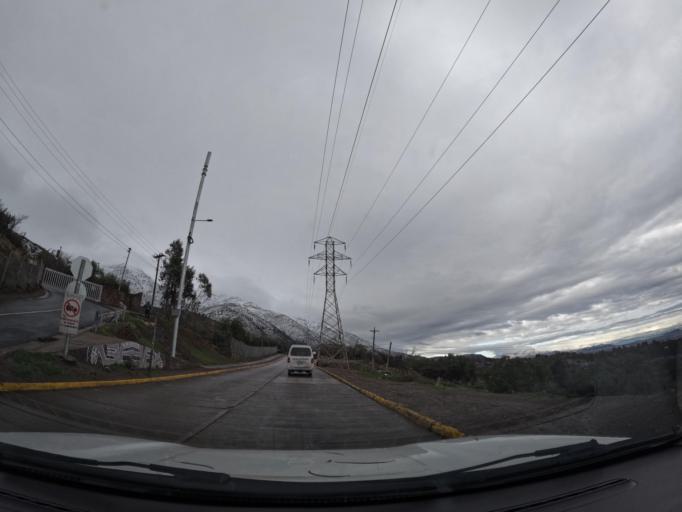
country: CL
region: Santiago Metropolitan
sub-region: Provincia de Santiago
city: Villa Presidente Frei, Nunoa, Santiago, Chile
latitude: -33.4892
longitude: -70.5196
